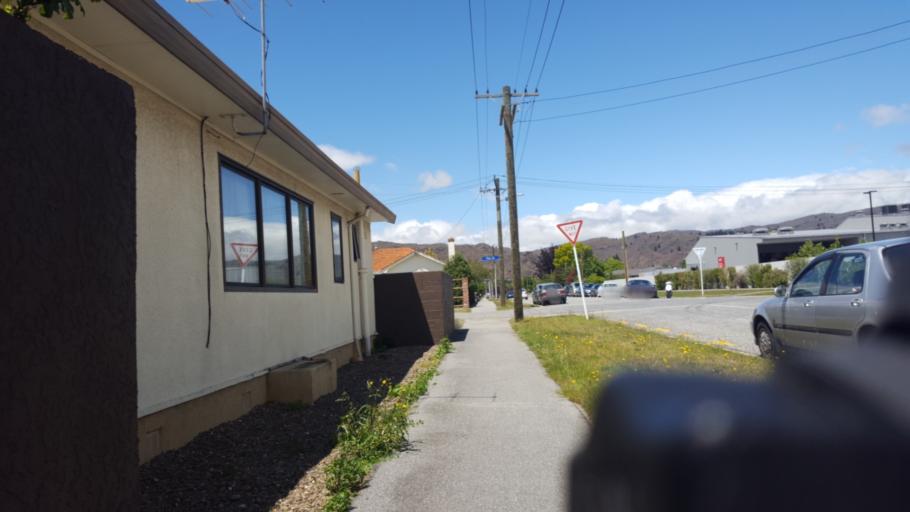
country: NZ
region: Otago
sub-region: Queenstown-Lakes District
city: Wanaka
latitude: -45.2487
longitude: 169.3875
